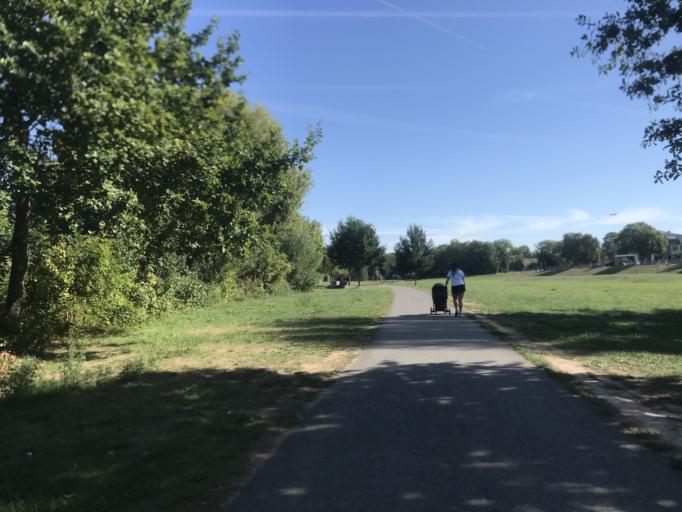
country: DE
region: Hesse
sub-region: Regierungsbezirk Darmstadt
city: Russelsheim
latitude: 49.9982
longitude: 8.4140
